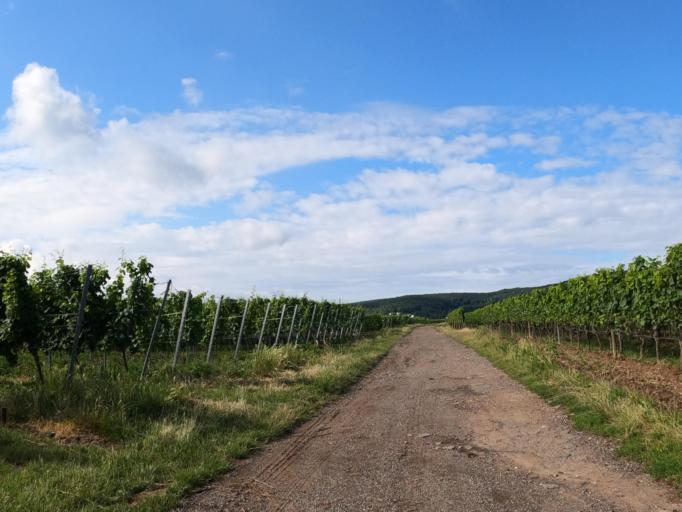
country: DE
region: Rheinland-Pfalz
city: Kleinkarlbach
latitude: 49.5355
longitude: 8.1596
